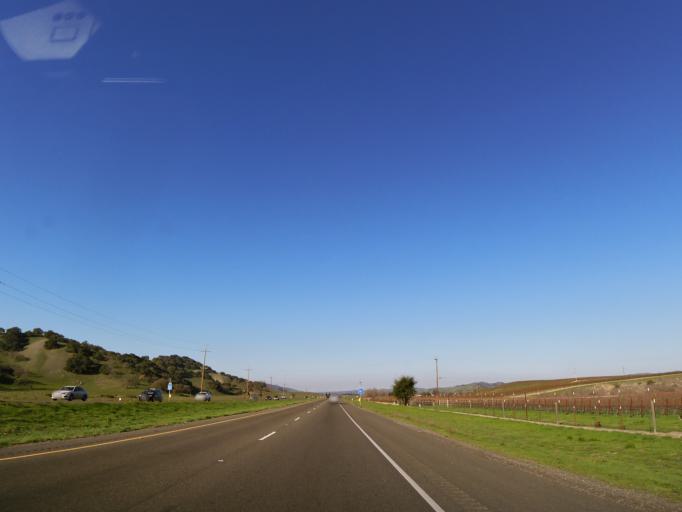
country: US
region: California
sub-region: Santa Barbara County
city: Los Alamos
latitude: 34.7263
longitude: -120.2223
